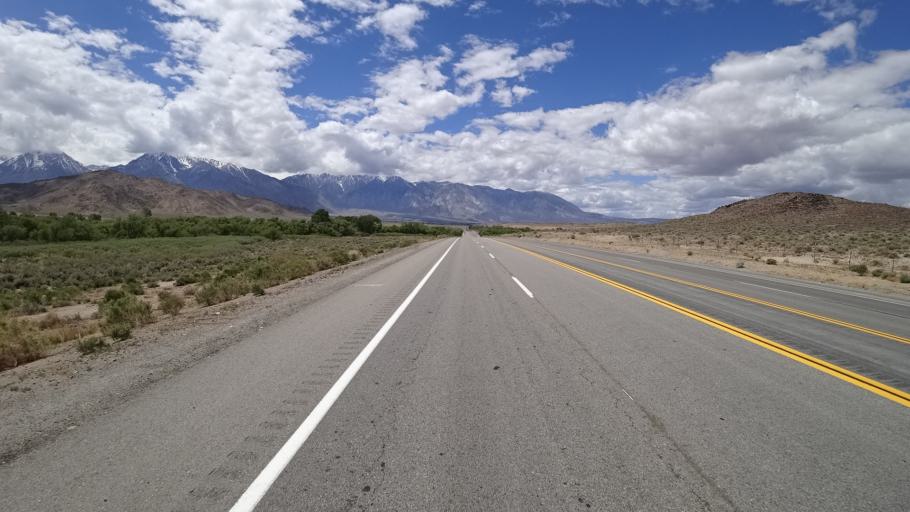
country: US
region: California
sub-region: Inyo County
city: West Bishop
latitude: 37.3842
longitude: -118.4865
